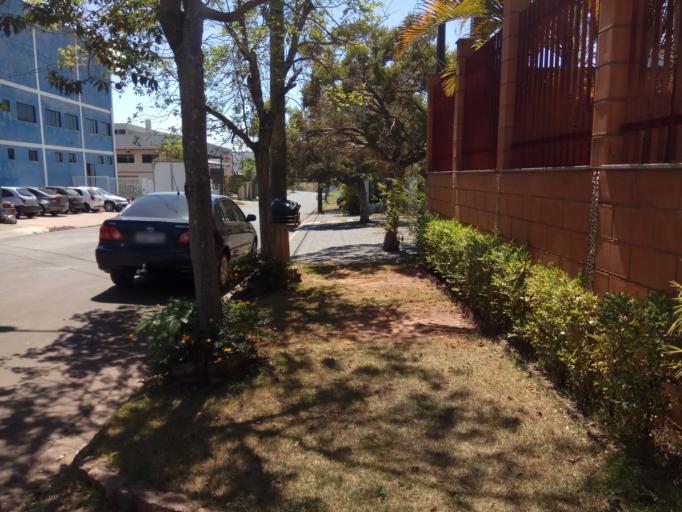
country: BR
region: Sao Paulo
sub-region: Piracicaba
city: Piracicaba
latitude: -22.7323
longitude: -47.5947
